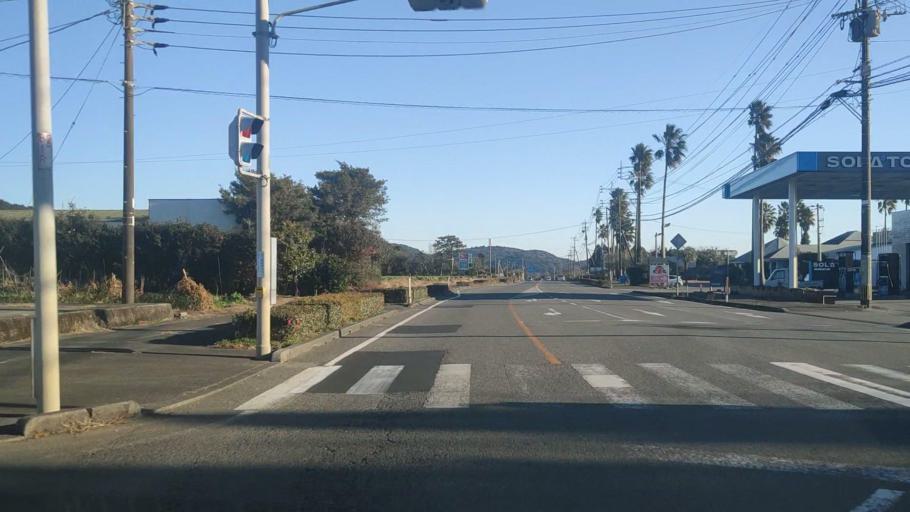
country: JP
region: Miyazaki
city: Takanabe
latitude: 32.3244
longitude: 131.5982
